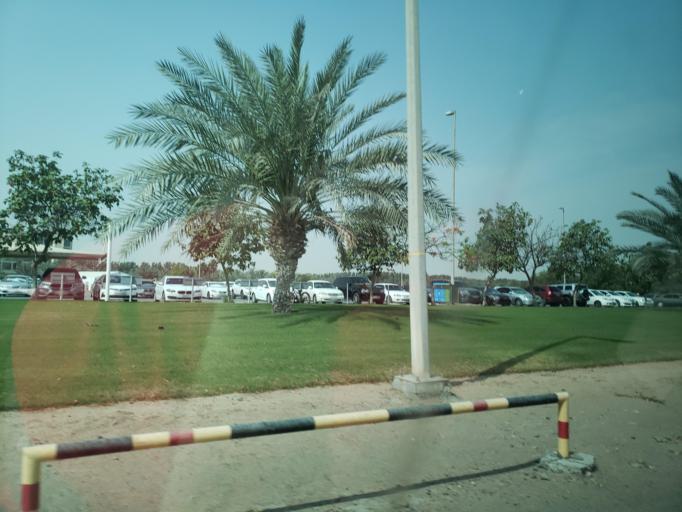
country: AE
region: Ash Shariqah
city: Sharjah
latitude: 25.3215
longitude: 55.5154
